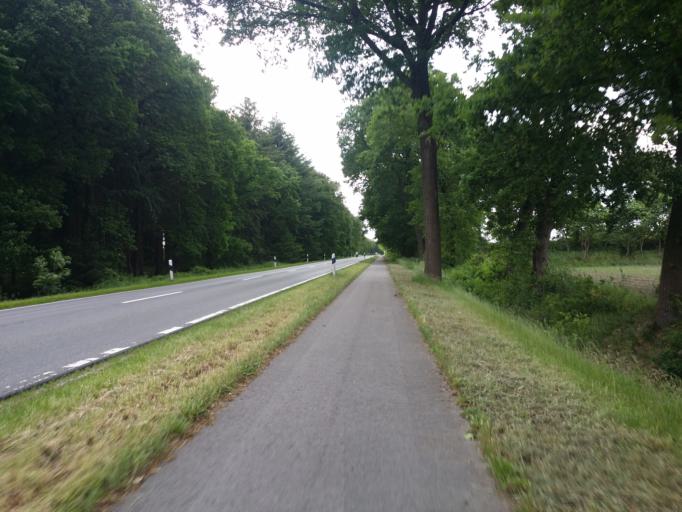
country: DE
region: Lower Saxony
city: Friedeburg
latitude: 53.5087
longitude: 7.8031
